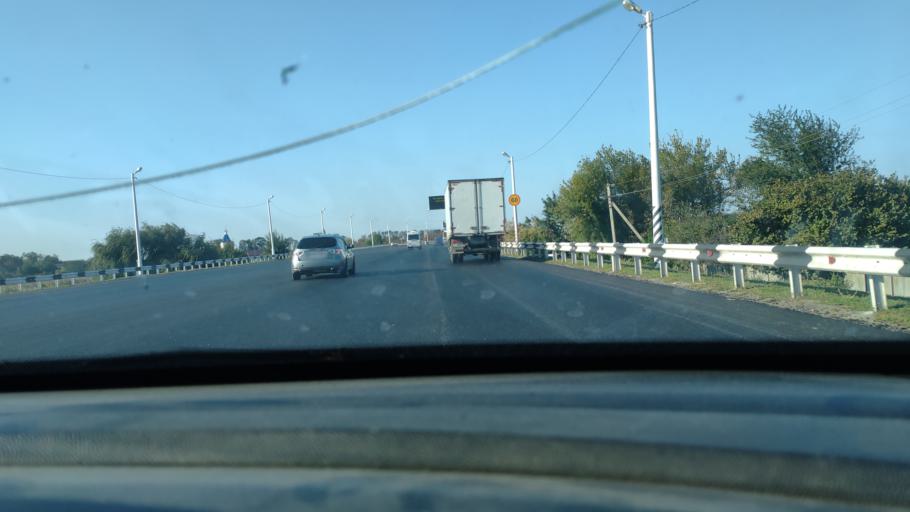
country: RU
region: Krasnodarskiy
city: Timashevsk
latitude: 45.5158
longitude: 38.9412
